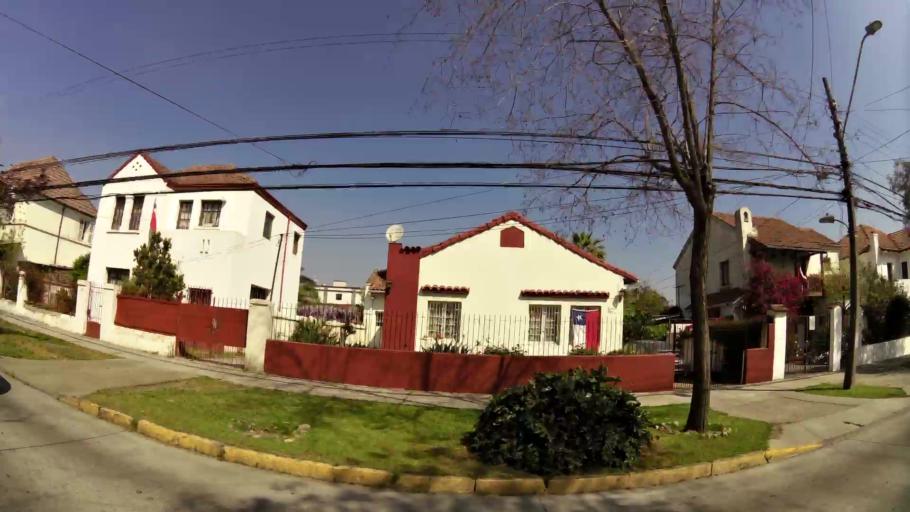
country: CL
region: Santiago Metropolitan
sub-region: Provincia de Santiago
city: Villa Presidente Frei, Nunoa, Santiago, Chile
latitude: -33.4576
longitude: -70.6123
